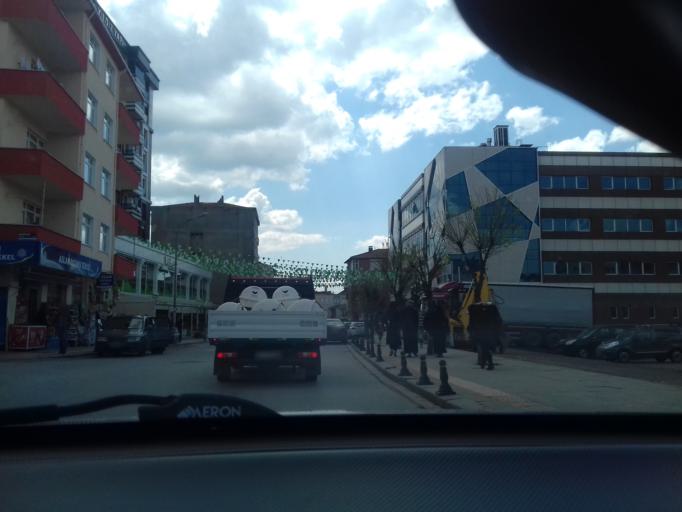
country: TR
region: Istanbul
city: Pendik
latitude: 40.8782
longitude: 29.2864
